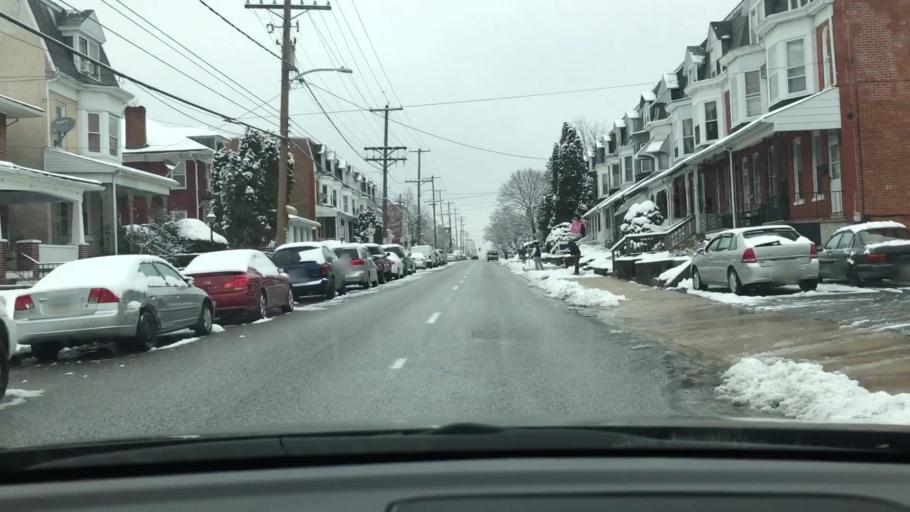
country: US
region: Pennsylvania
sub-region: York County
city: West York
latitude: 39.9548
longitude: -76.7473
